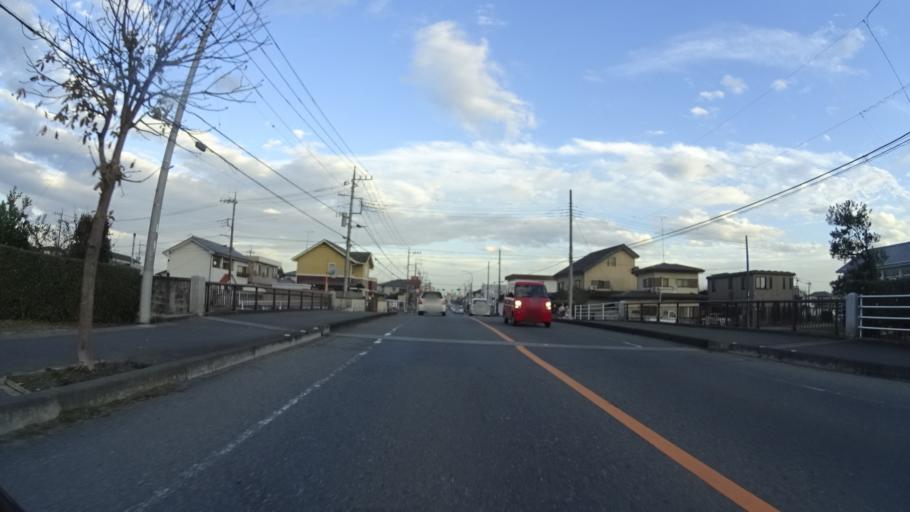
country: JP
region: Tochigi
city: Tochigi
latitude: 36.3912
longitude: 139.7308
